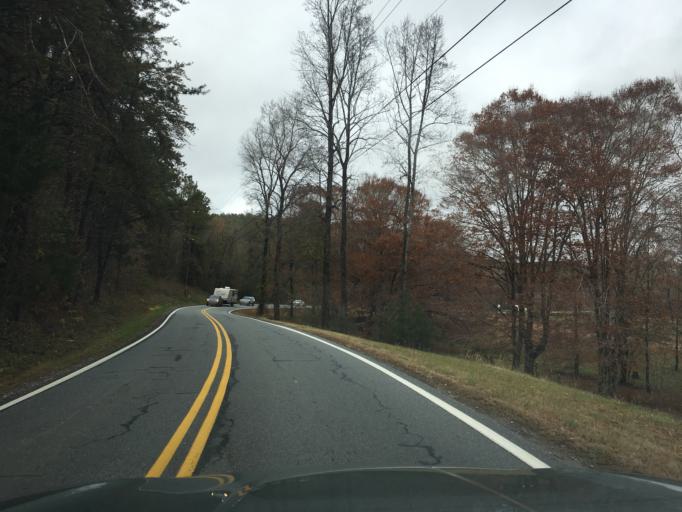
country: US
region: North Carolina
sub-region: Rutherford County
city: Rutherfordton
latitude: 35.2808
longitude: -82.0302
